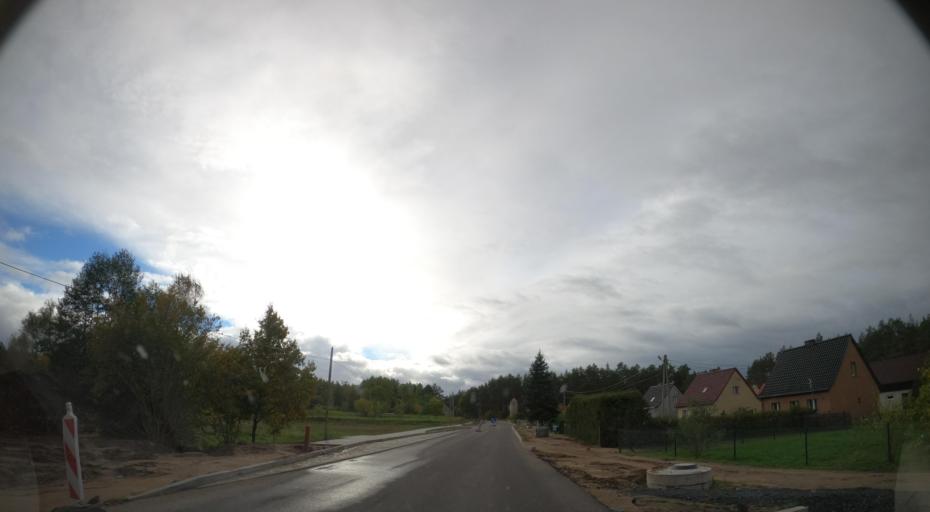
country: PL
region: West Pomeranian Voivodeship
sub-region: Powiat goleniowski
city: Stepnica
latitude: 53.7120
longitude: 14.6683
